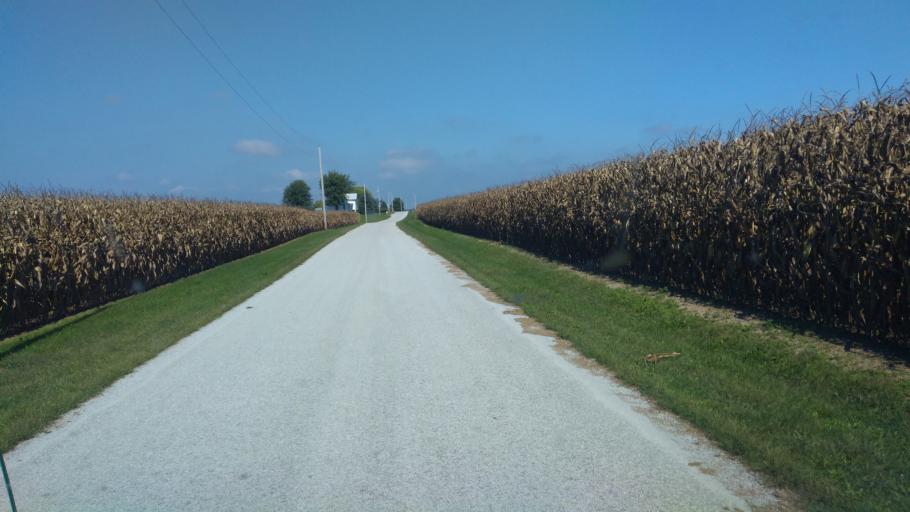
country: US
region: Ohio
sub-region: Hardin County
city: Kenton
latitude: 40.7004
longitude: -83.6002
